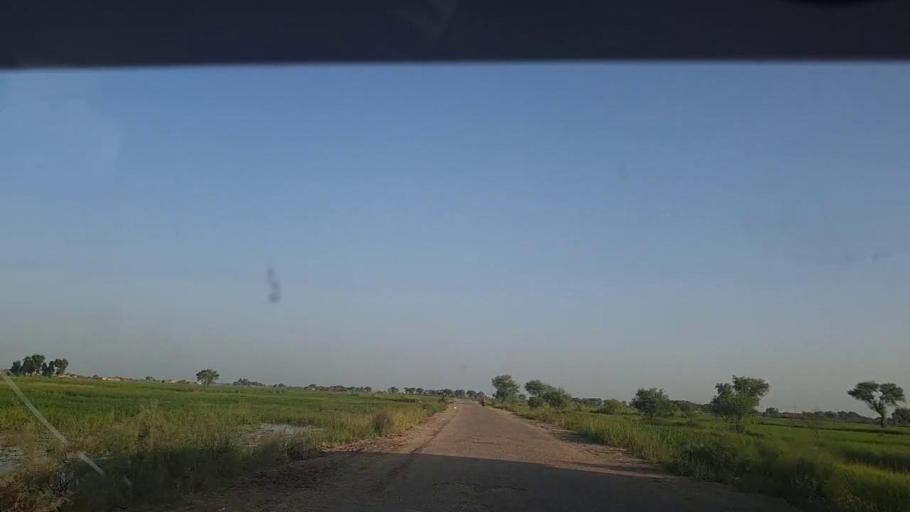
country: PK
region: Sindh
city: Thul
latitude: 28.1898
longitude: 68.8720
